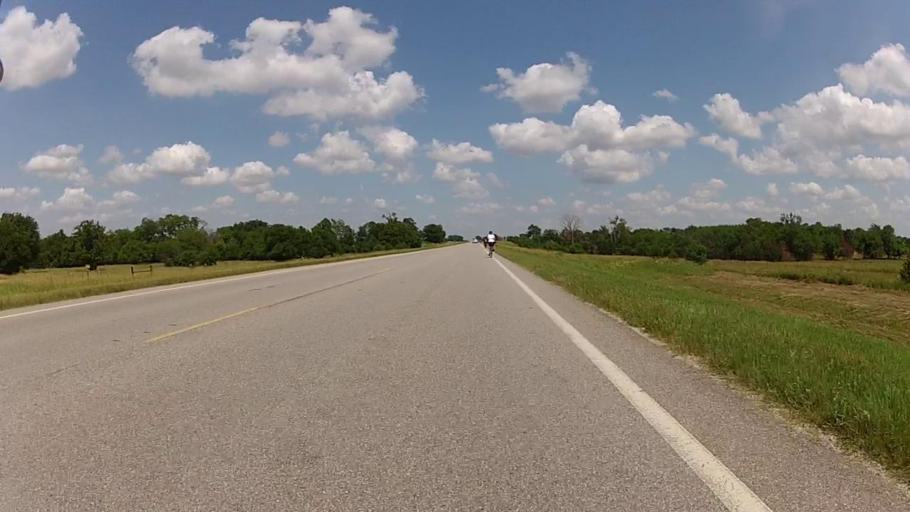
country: US
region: Kansas
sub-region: Labette County
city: Altamont
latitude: 37.1931
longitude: -95.2252
